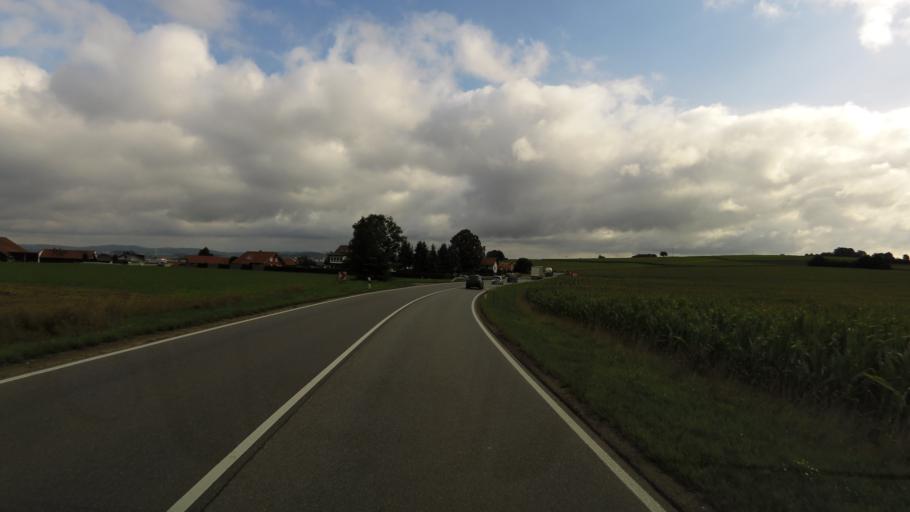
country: DE
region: Bavaria
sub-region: Upper Palatinate
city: Cham
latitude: 49.1878
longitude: 12.6532
